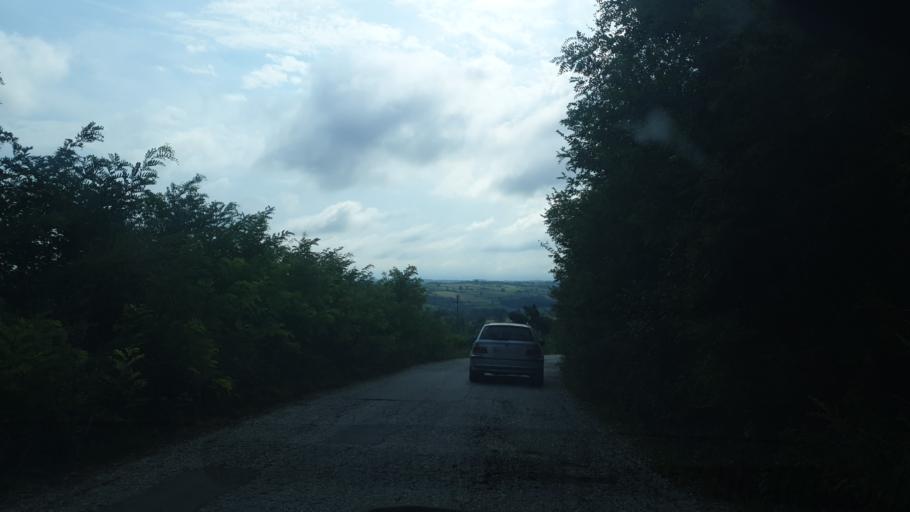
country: RS
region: Central Serbia
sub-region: Sumadijski Okrug
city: Kragujevac
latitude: 44.0972
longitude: 20.7836
